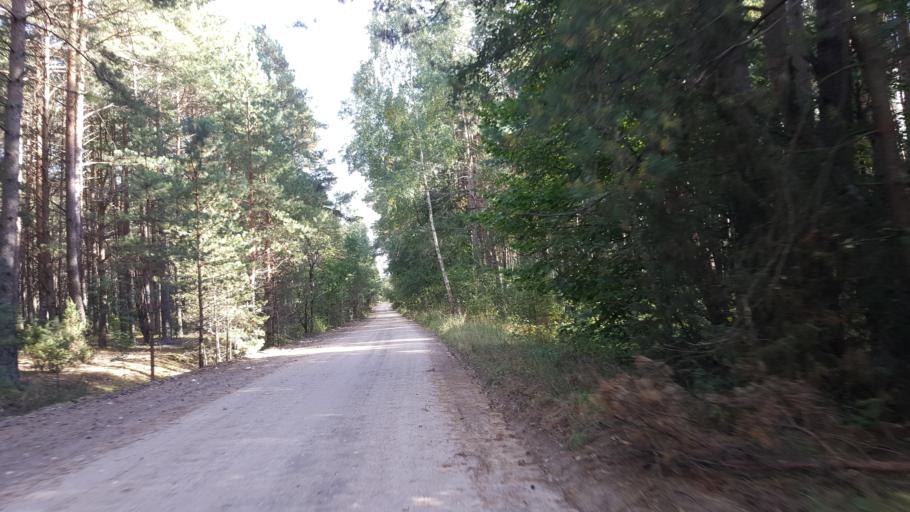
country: BY
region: Brest
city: Kamyanyets
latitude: 52.4368
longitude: 23.9409
